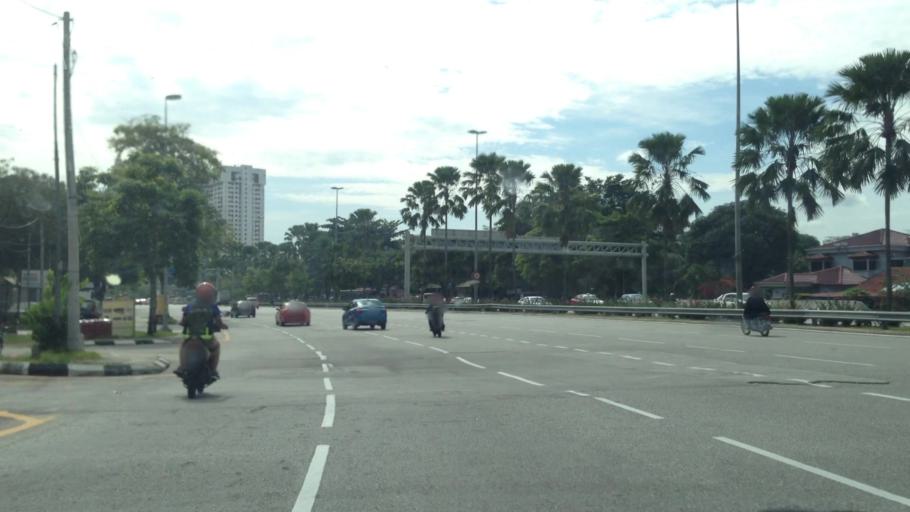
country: MY
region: Kuala Lumpur
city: Kuala Lumpur
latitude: 3.0819
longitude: 101.6674
